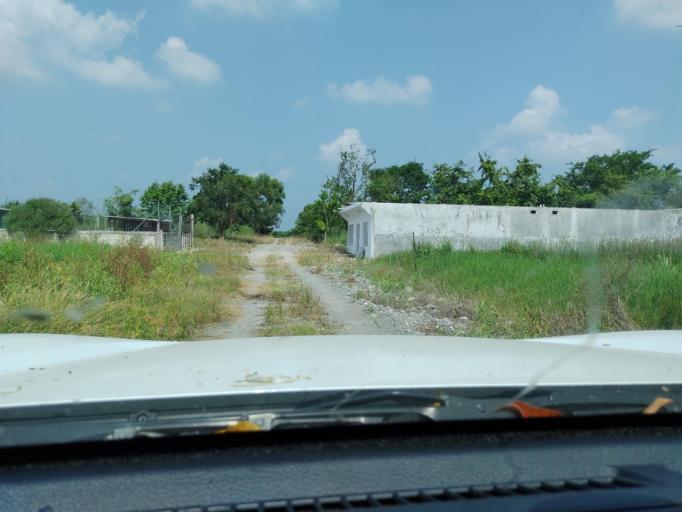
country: MX
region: Veracruz
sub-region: Martinez de la Torre
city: El Progreso
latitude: 20.0692
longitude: -97.0084
